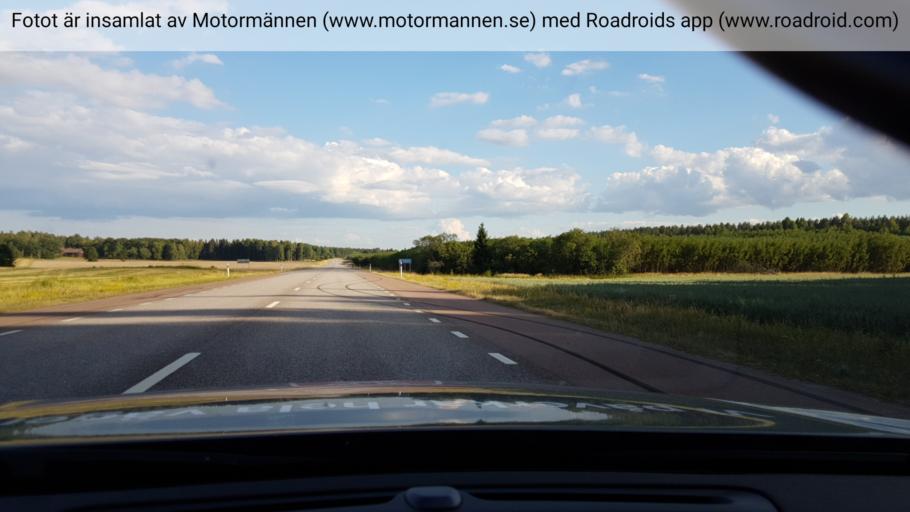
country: SE
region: Uppsala
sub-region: Heby Kommun
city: Morgongava
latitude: 59.8662
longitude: 16.9260
